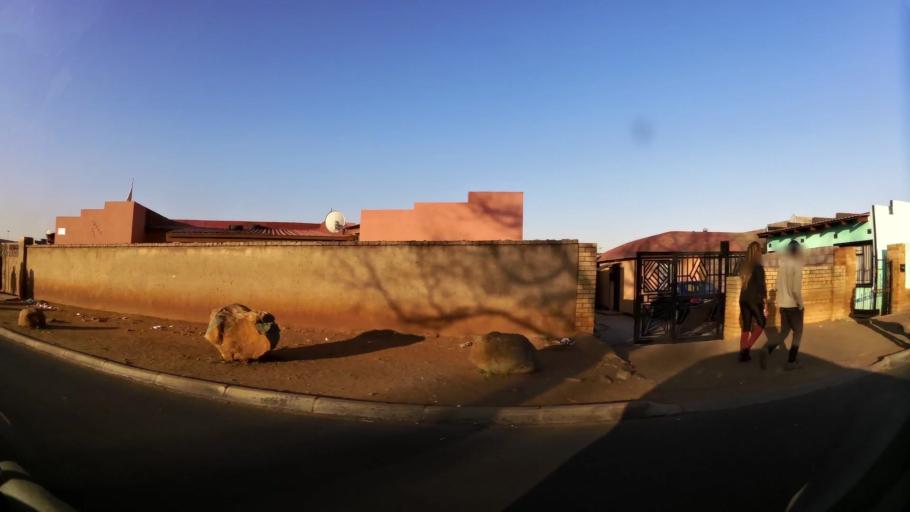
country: ZA
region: Gauteng
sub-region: City of Johannesburg Metropolitan Municipality
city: Soweto
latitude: -26.2485
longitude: 27.8777
